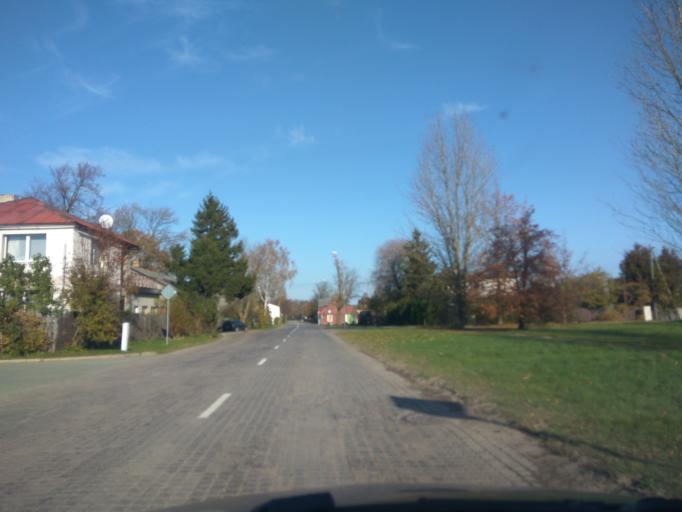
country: LV
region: Ventspils
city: Ventspils
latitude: 57.3710
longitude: 21.5687
